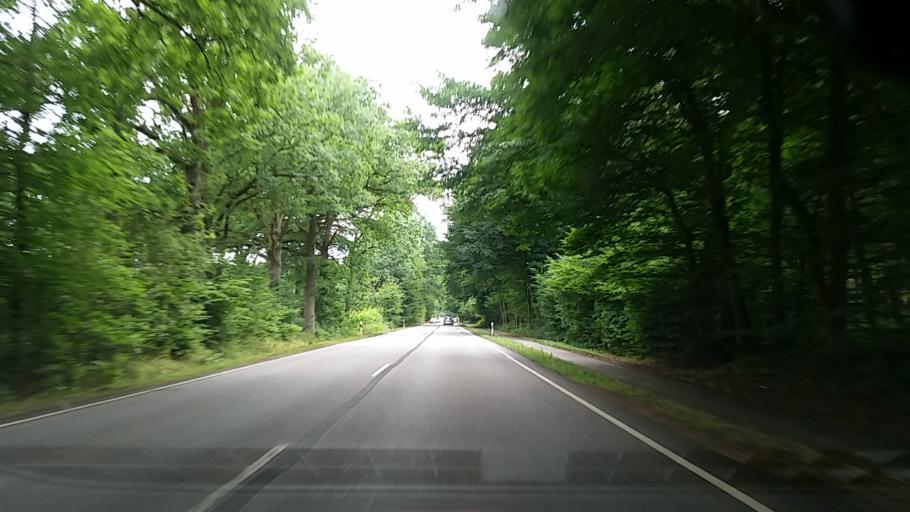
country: DE
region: Hamburg
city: Duvenstedt
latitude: 53.7347
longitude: 10.1110
